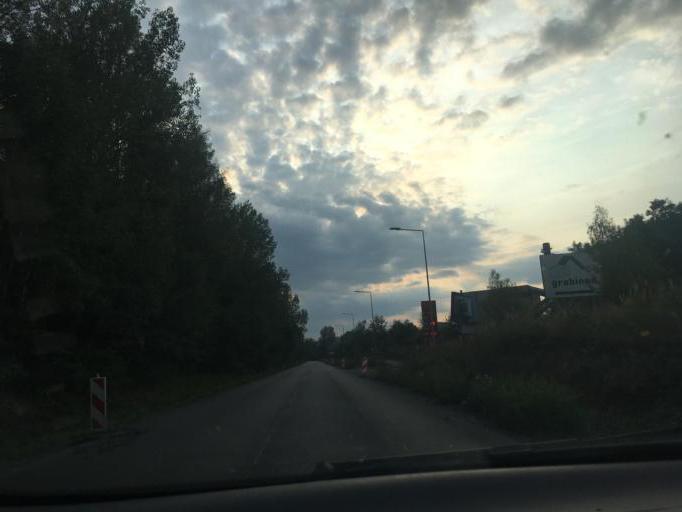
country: PL
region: Lower Silesian Voivodeship
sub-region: Powiat klodzki
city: Bozkow
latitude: 50.5366
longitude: 16.5734
